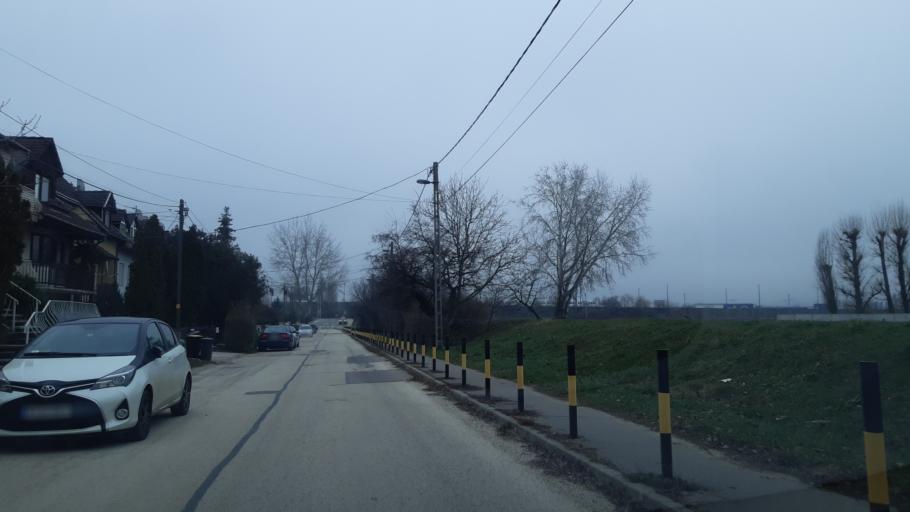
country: HU
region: Pest
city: Budaors
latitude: 47.4570
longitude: 18.9718
